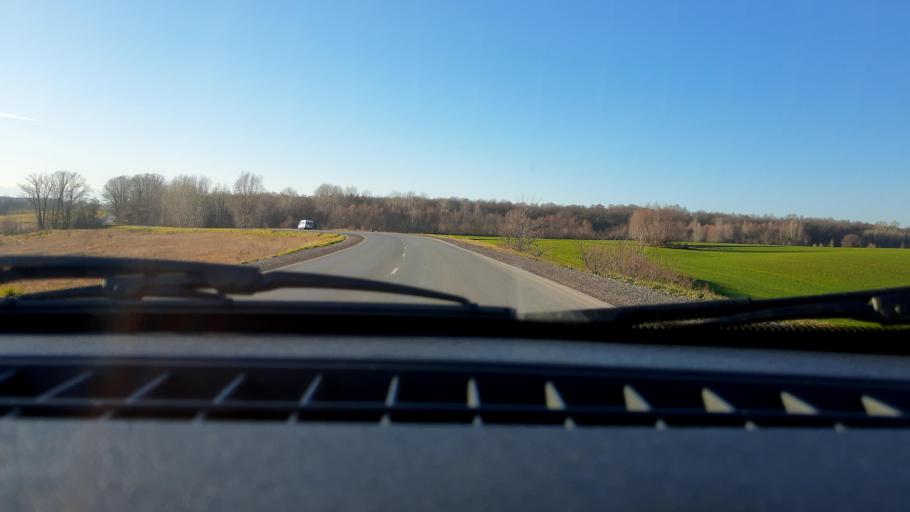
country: RU
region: Bashkortostan
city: Mikhaylovka
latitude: 54.8334
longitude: 55.9398
